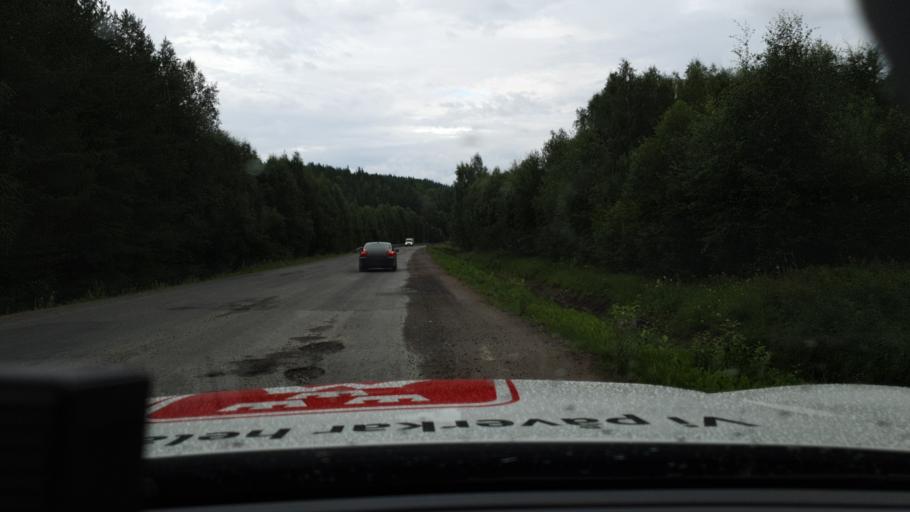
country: SE
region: Norrbotten
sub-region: Bodens Kommun
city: Boden
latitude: 65.8473
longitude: 21.5925
